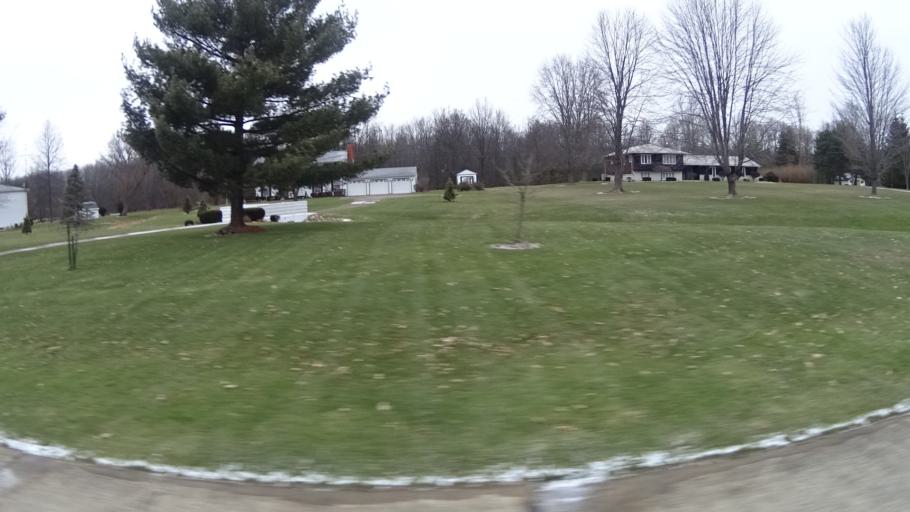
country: US
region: Ohio
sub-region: Lorain County
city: Grafton
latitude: 41.2882
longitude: -82.0470
